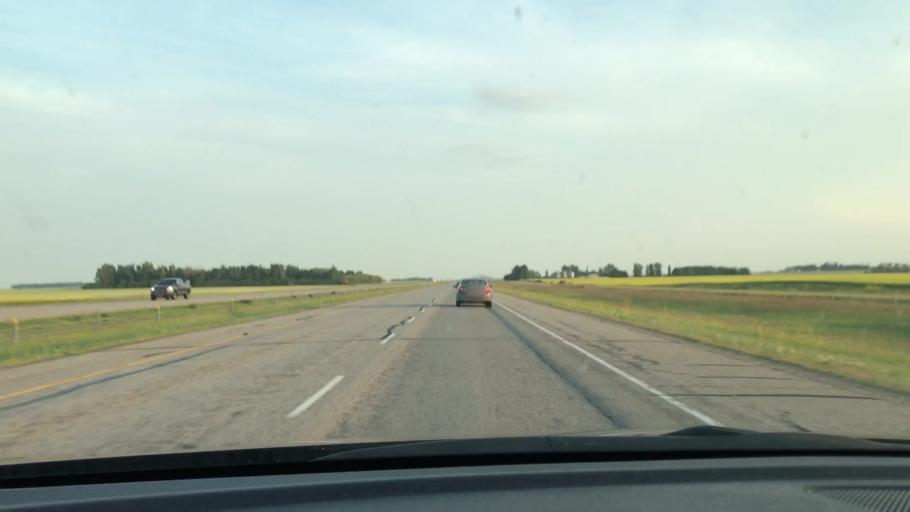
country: CA
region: Alberta
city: Olds
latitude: 51.8408
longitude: -114.0257
